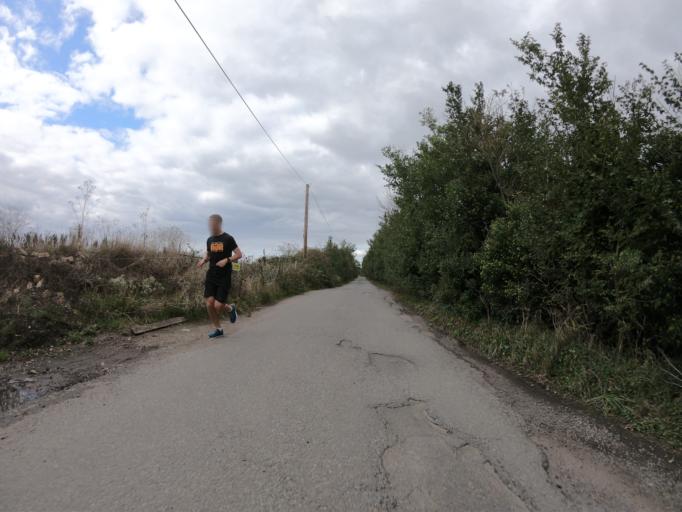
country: GB
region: England
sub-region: Kent
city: Dartford
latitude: 51.4655
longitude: 0.2161
